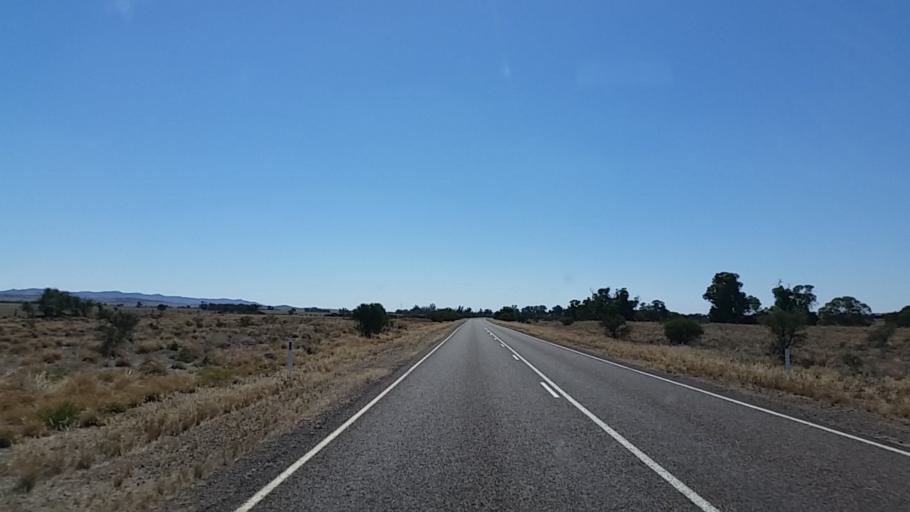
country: AU
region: South Australia
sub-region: Flinders Ranges
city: Quorn
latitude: -32.4878
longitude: 138.5456
